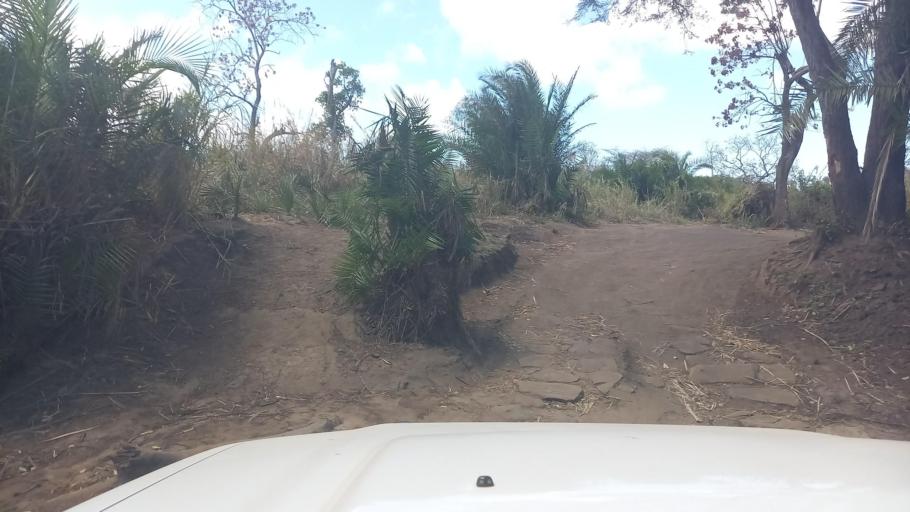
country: MZ
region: Cabo Delgado
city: Pemba
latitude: -13.4233
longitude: 40.4800
